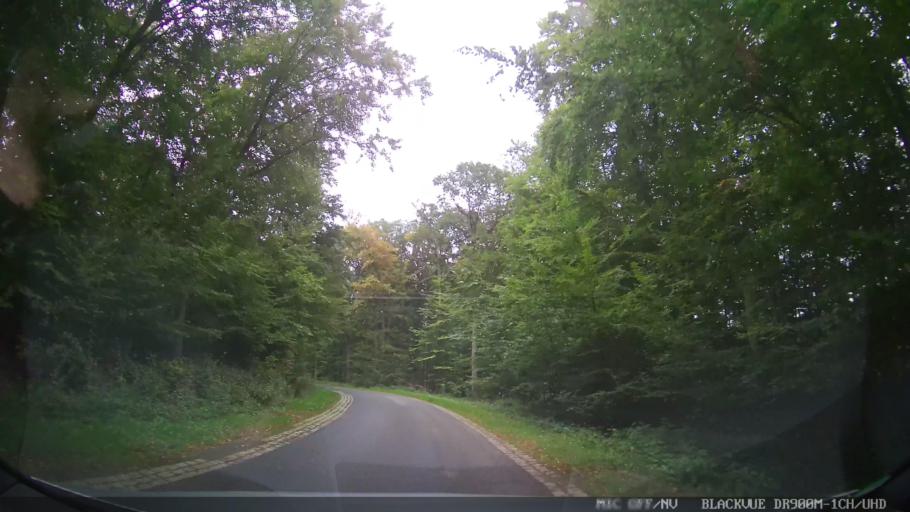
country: DE
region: Schleswig-Holstein
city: Gromitz
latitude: 54.1826
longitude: 10.9700
